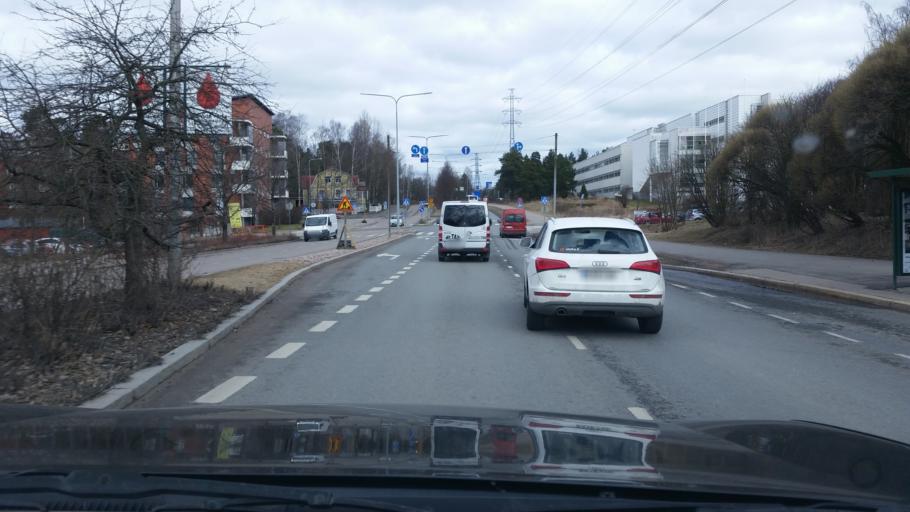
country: FI
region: Uusimaa
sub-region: Helsinki
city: Teekkarikylae
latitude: 60.2103
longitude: 24.8804
